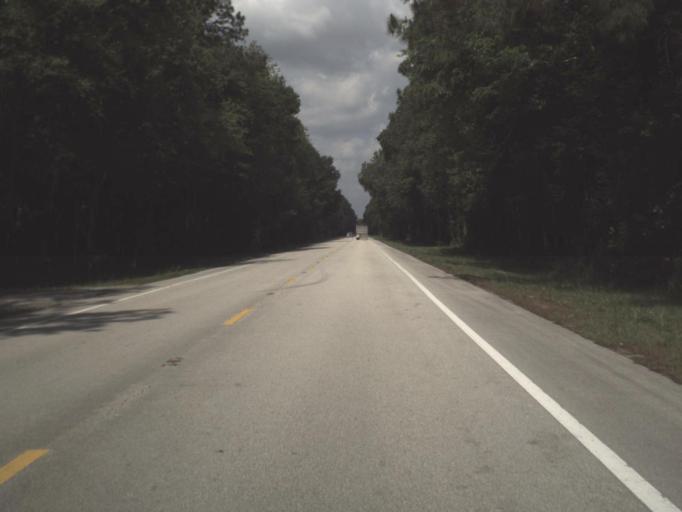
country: US
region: Florida
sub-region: Saint Johns County
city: Saint Augustine Shores
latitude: 29.7271
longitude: -81.4033
